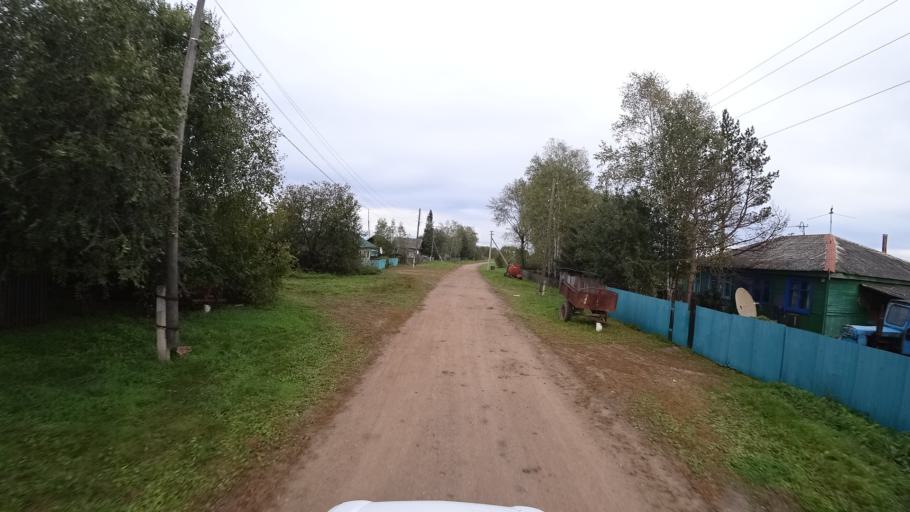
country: RU
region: Amur
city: Arkhara
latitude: 49.4359
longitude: 130.2693
